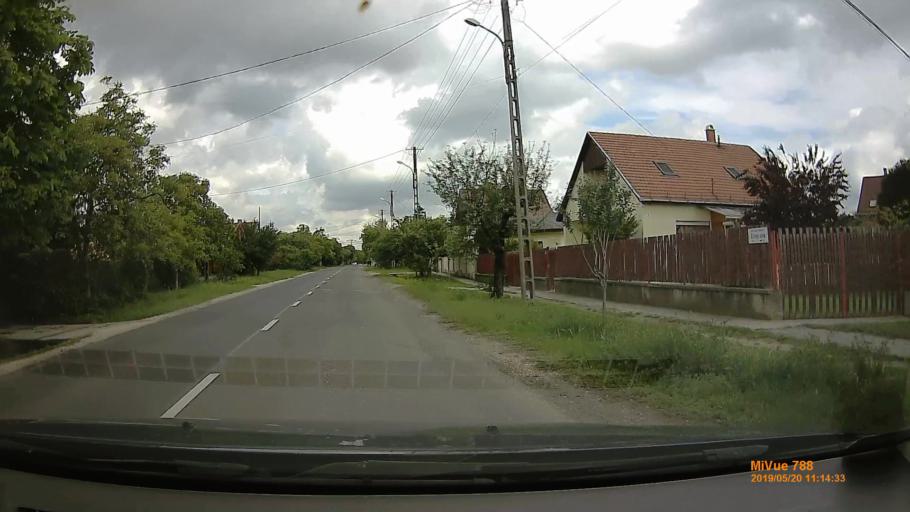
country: HU
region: Pest
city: Ecser
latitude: 47.4621
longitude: 19.2983
